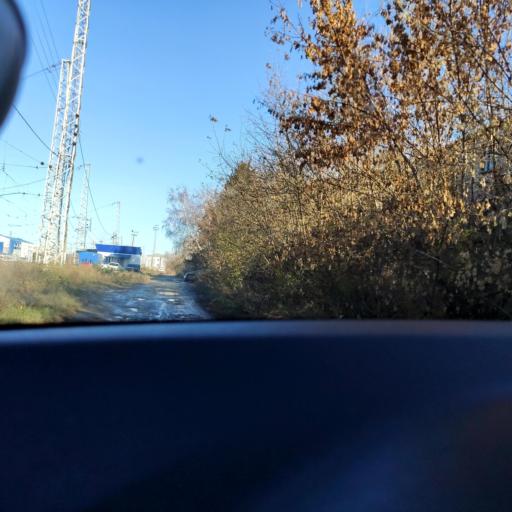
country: RU
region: Samara
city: Samara
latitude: 53.2080
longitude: 50.2591
